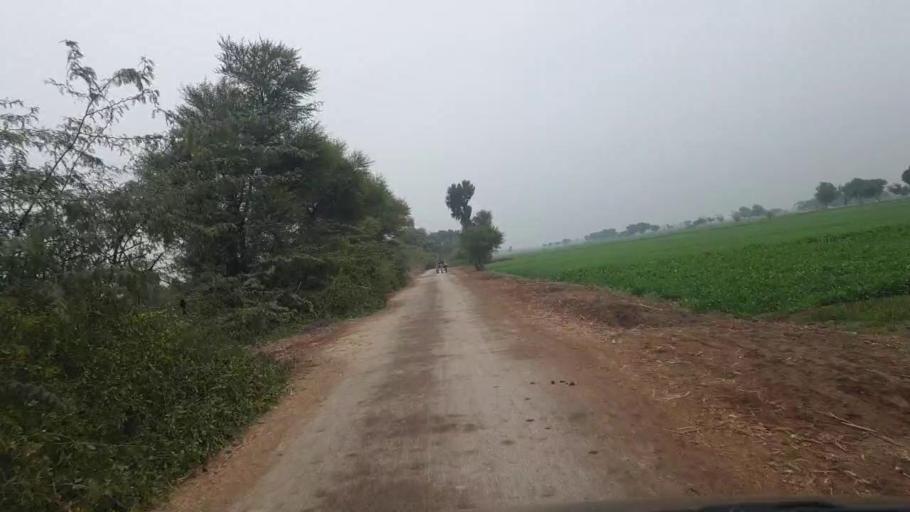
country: PK
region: Sindh
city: Tando Adam
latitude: 25.8478
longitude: 68.6849
